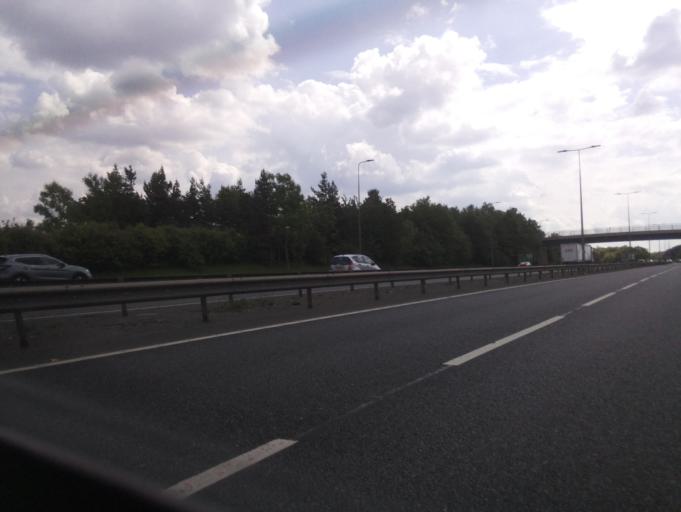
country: GB
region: England
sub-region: Redcar and Cleveland
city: Thornaby-on-Tees
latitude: 54.5349
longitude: -1.2794
